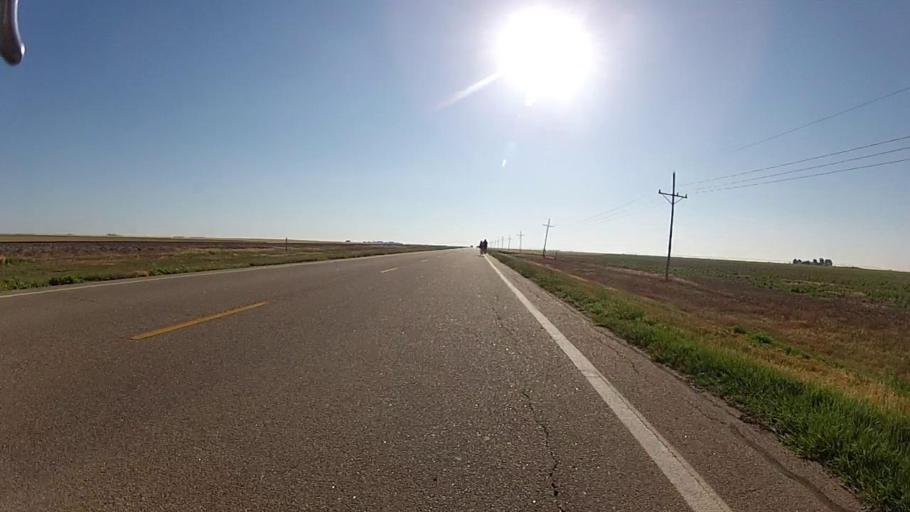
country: US
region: Kansas
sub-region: Haskell County
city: Sublette
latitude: 37.5183
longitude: -100.7184
